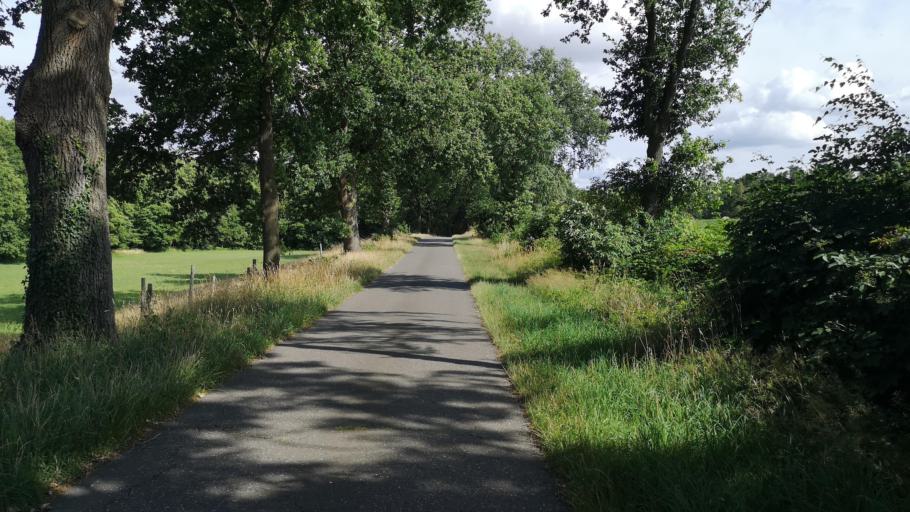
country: DE
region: Lower Saxony
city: Thomasburg
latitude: 53.2259
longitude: 10.6608
